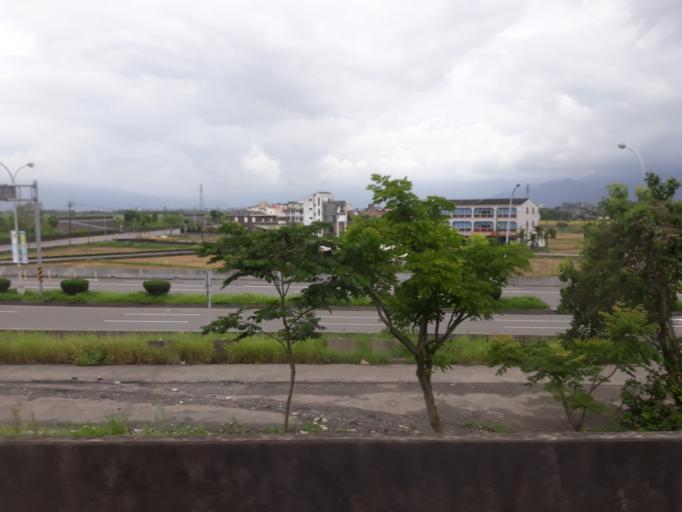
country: TW
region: Taiwan
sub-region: Yilan
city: Yilan
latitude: 24.7196
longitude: 121.7712
